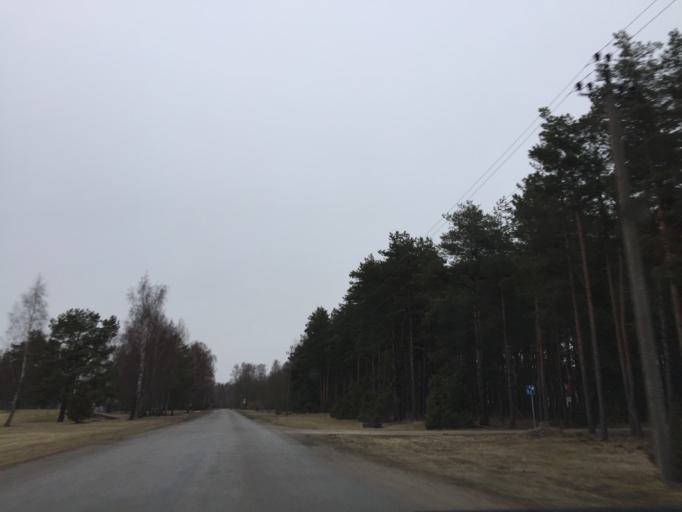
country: EE
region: Laeaene
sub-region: Lihula vald
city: Lihula
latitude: 58.6247
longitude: 23.6323
